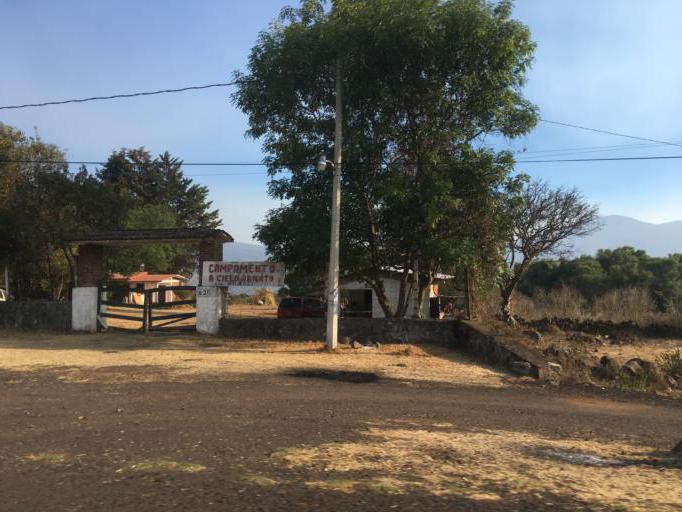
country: MX
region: Michoacan
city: Santa Fe de la Laguna
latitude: 19.6719
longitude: -101.5631
